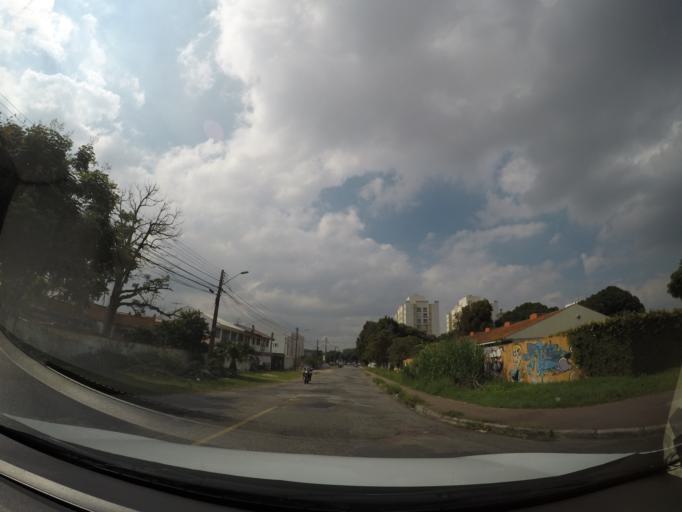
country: BR
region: Parana
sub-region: Sao Jose Dos Pinhais
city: Sao Jose dos Pinhais
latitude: -25.4948
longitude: -49.2434
